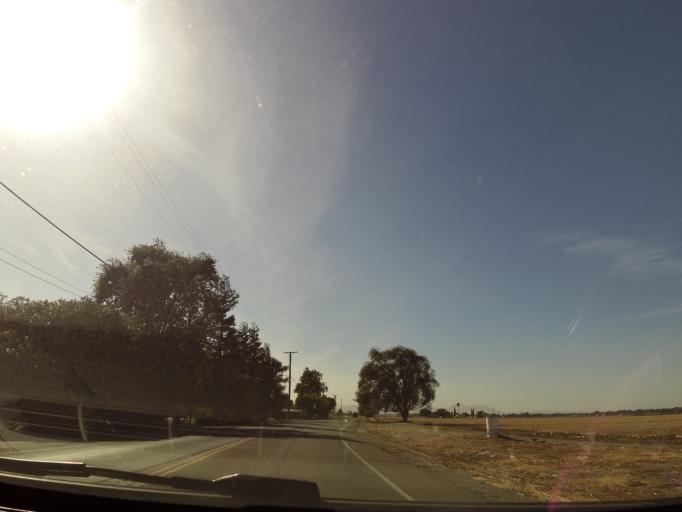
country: US
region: California
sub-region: San Joaquin County
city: Tracy
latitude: 37.7905
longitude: -121.4390
